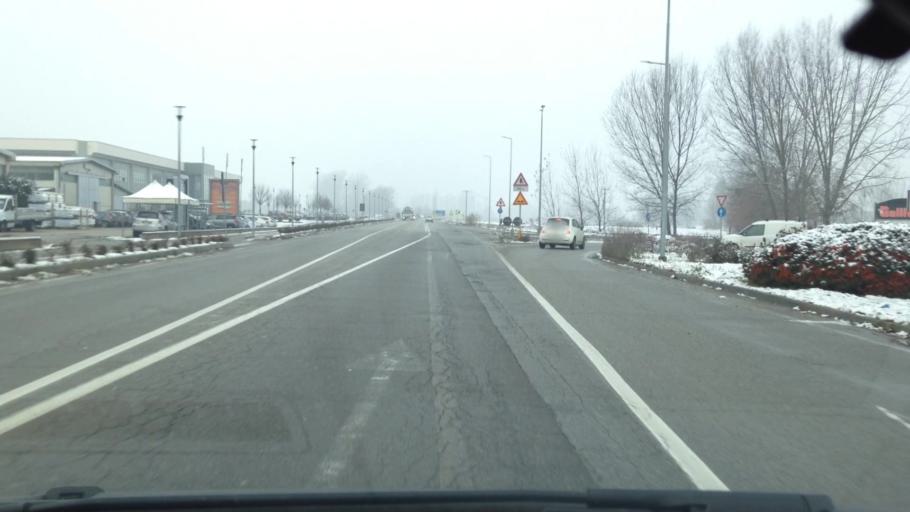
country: IT
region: Piedmont
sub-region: Provincia di Asti
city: Montegrosso
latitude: 44.8206
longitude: 8.2308
